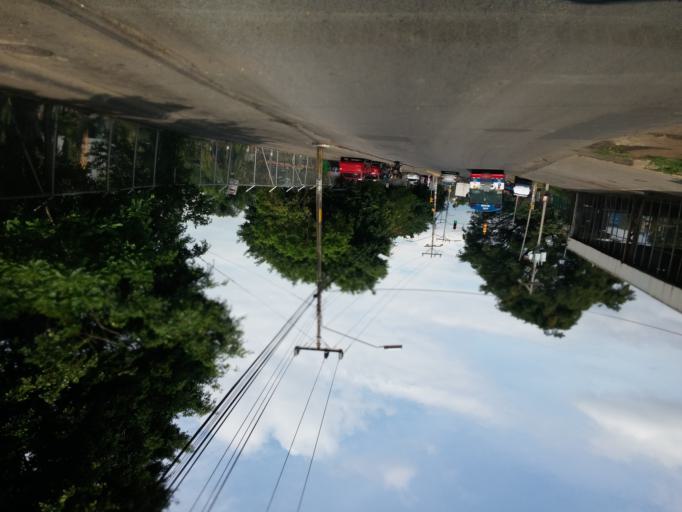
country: CR
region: Alajuela
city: Alajuela
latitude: 10.0086
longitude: -84.2112
